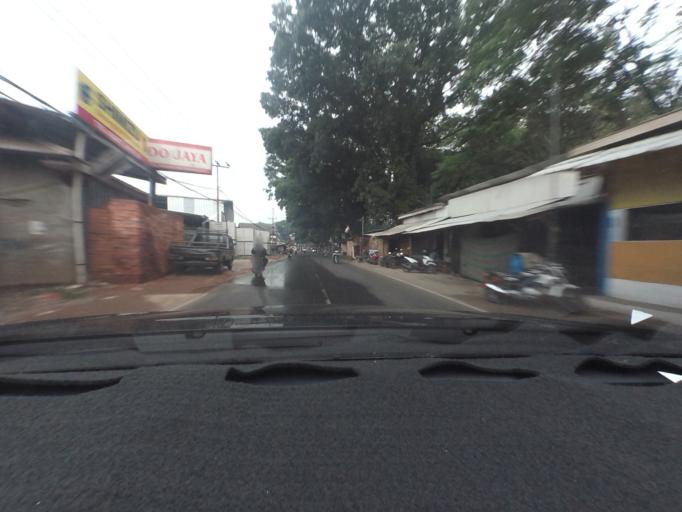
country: ID
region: West Java
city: Cicurug
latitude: -6.8063
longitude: 106.7698
